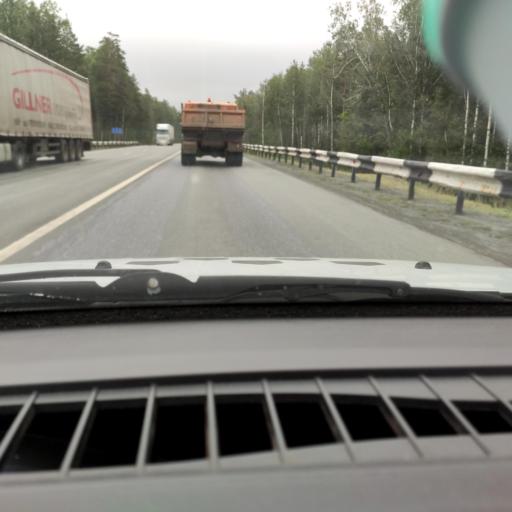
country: RU
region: Chelyabinsk
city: Syrostan
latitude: 55.0174
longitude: 59.7813
